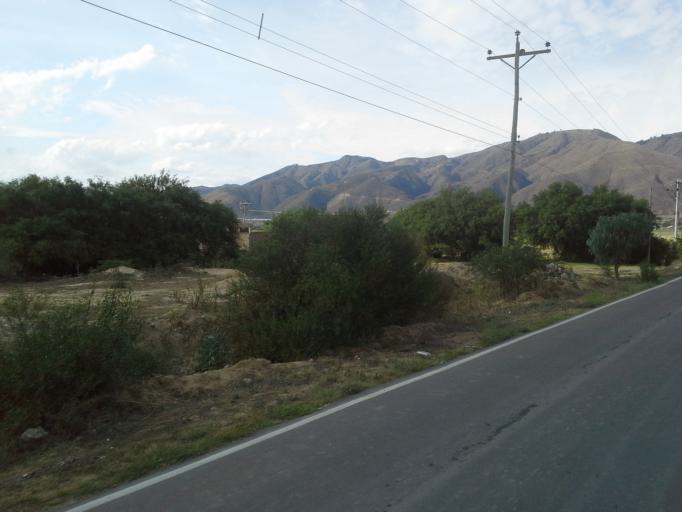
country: BO
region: Cochabamba
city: Tarata
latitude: -17.5612
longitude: -66.0089
